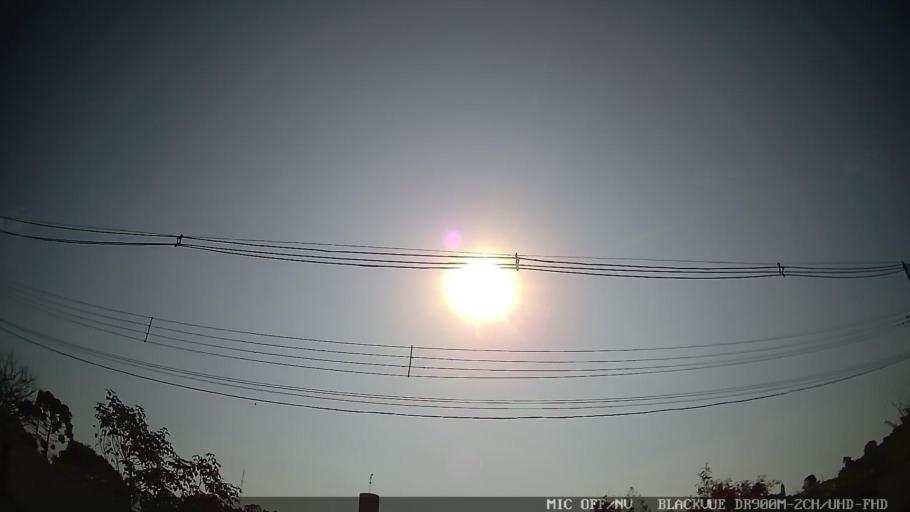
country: BR
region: Sao Paulo
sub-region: Itatiba
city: Itatiba
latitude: -23.0009
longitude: -46.8483
